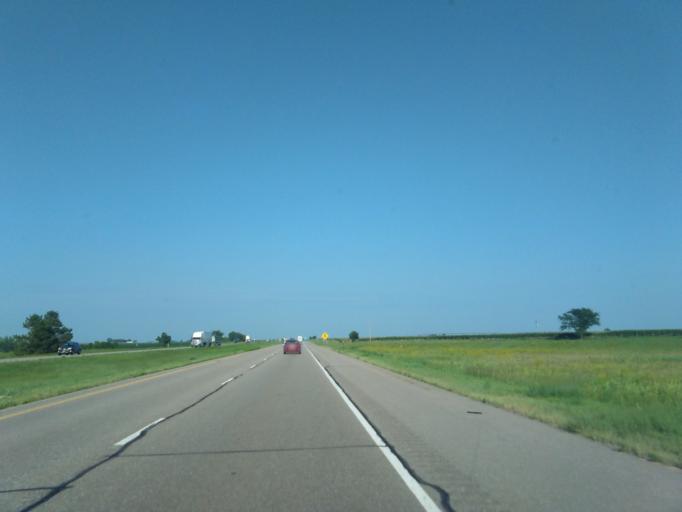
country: US
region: Nebraska
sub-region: Hamilton County
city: Aurora
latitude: 40.8221
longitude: -98.1491
